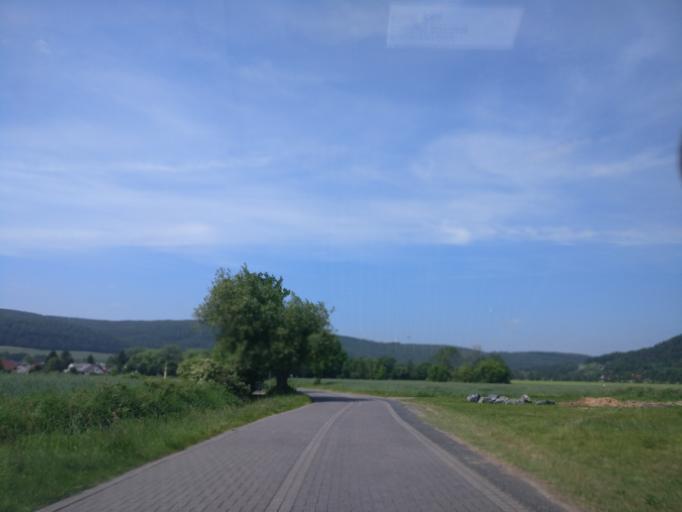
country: DE
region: Lower Saxony
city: Hannoversch Munden
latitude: 51.4390
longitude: 9.6565
